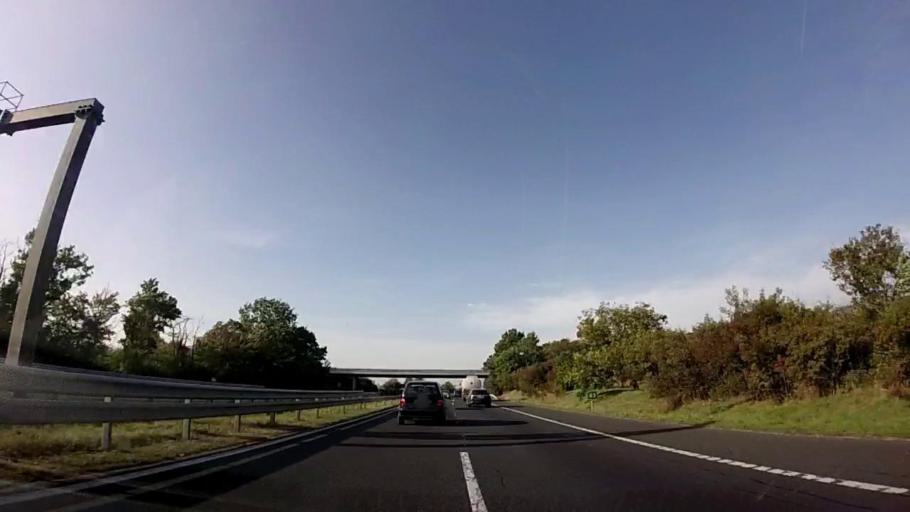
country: HU
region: Fejer
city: Velence
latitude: 47.2491
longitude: 18.6592
